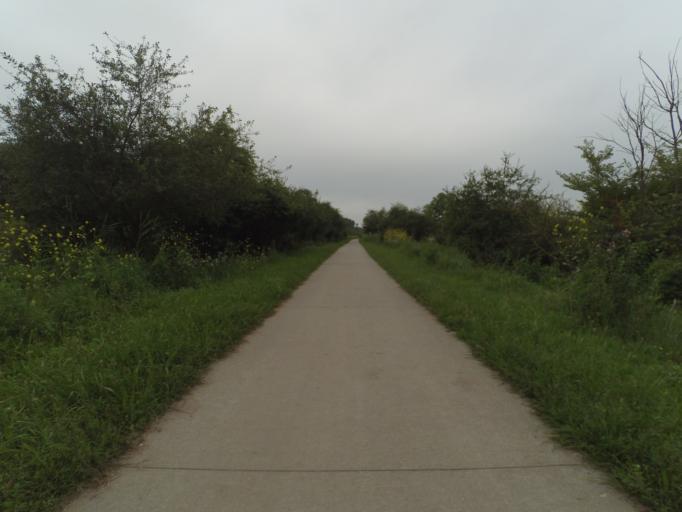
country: NL
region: Flevoland
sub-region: Gemeente Almere
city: Almere Stad
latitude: 52.4233
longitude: 5.2766
